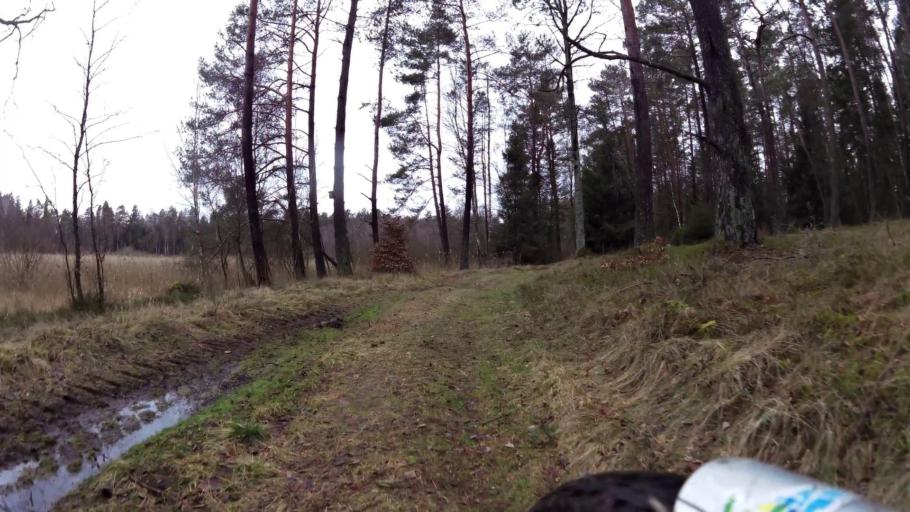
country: PL
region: Pomeranian Voivodeship
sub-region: Powiat bytowski
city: Borzytuchom
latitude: 54.2642
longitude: 17.3464
